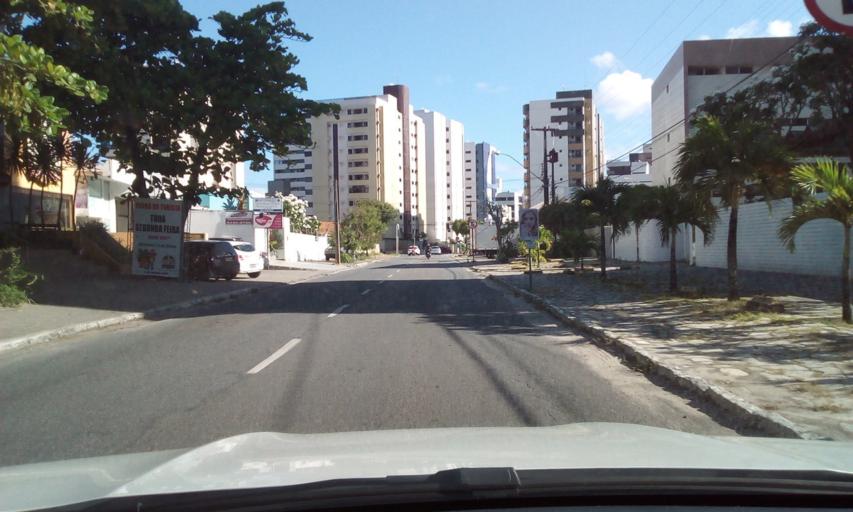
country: BR
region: Paraiba
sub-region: Joao Pessoa
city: Joao Pessoa
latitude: -7.1128
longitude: -34.8256
